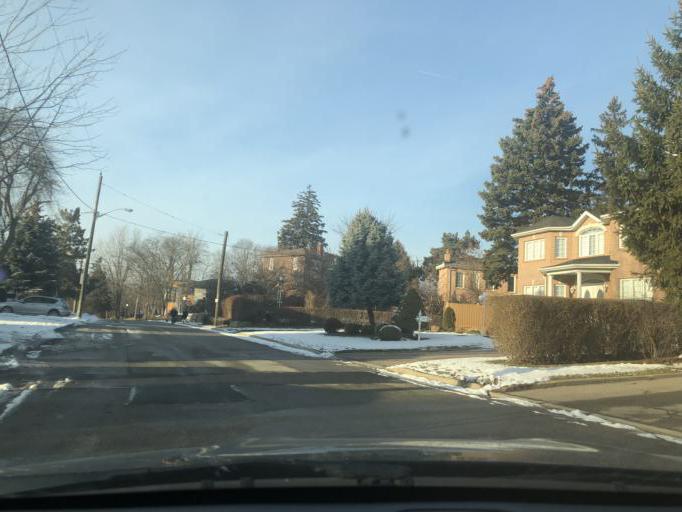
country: CA
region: Ontario
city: Toronto
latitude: 43.6935
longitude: -79.4775
